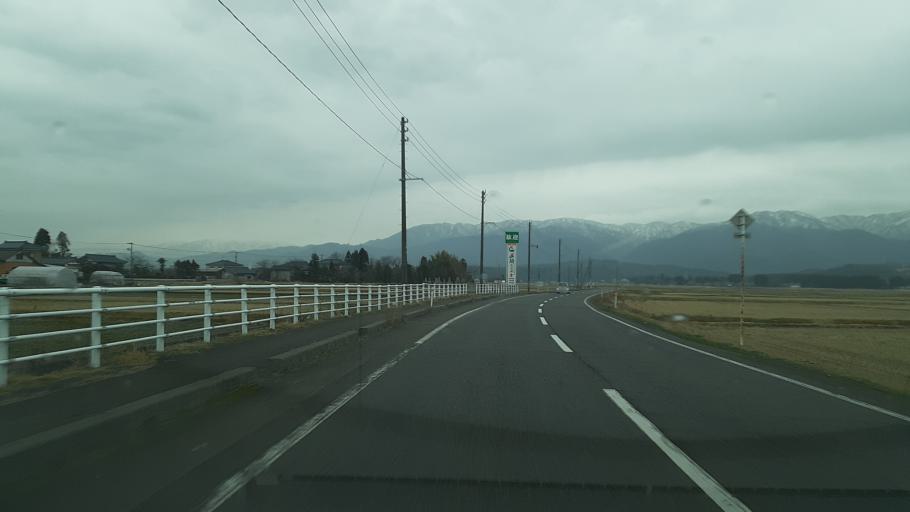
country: JP
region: Niigata
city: Suibara
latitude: 37.8332
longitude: 139.2439
